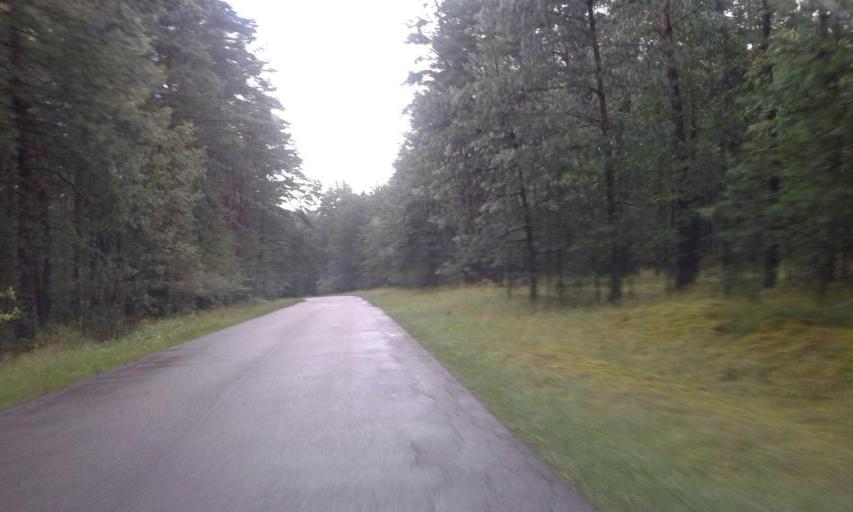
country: PL
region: West Pomeranian Voivodeship
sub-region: Powiat szczecinecki
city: Borne Sulinowo
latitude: 53.5514
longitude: 16.5149
